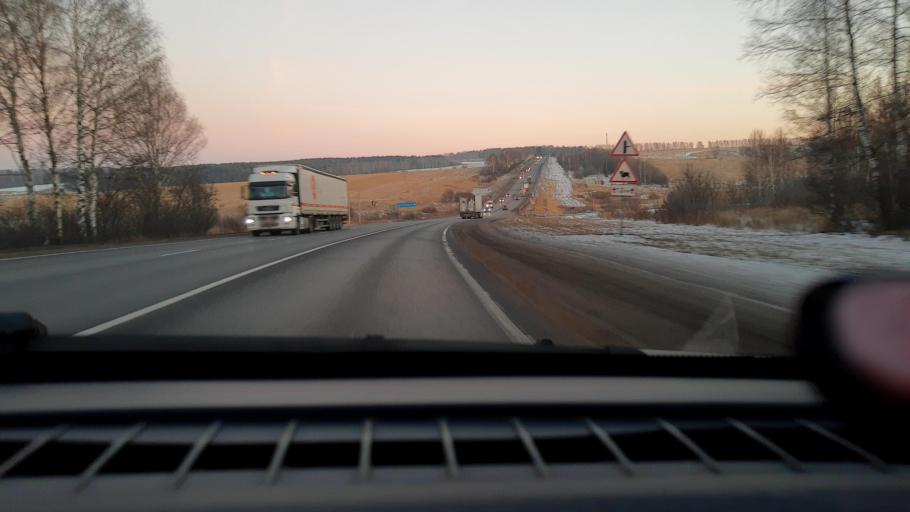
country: RU
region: Nizjnij Novgorod
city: Pamyat' Parizhskoy Kommuny
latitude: 56.0385
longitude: 44.4836
